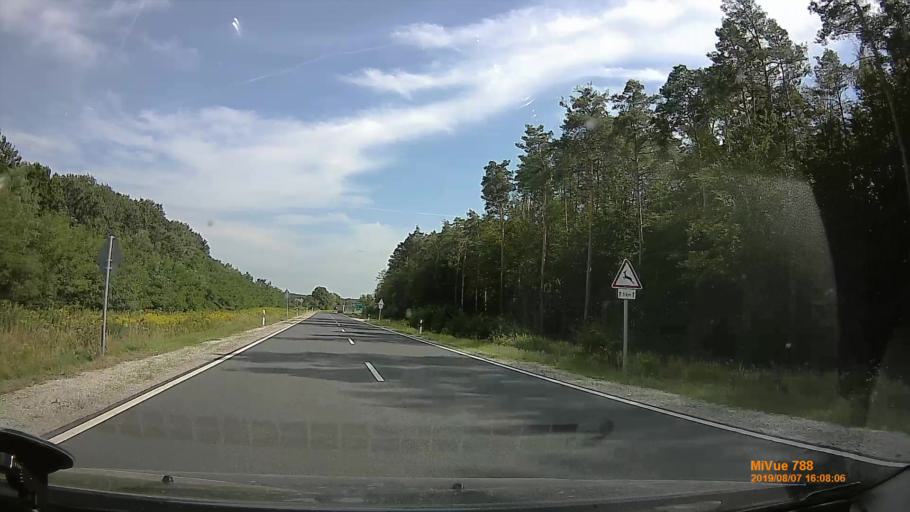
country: HU
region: Zala
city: Zalalovo
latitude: 46.9129
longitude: 16.5997
